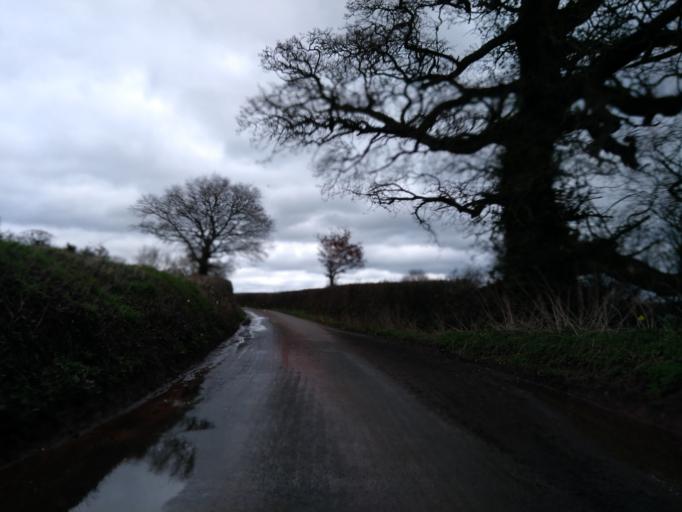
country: GB
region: England
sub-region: Devon
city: Crediton
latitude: 50.7879
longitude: -3.5741
